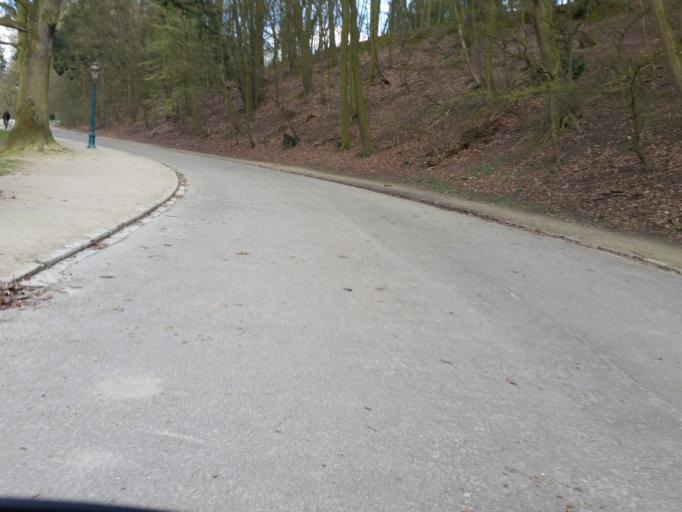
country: BE
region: Flanders
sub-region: Provincie Vlaams-Brabant
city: Kraainem
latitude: 50.8239
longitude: 4.4245
